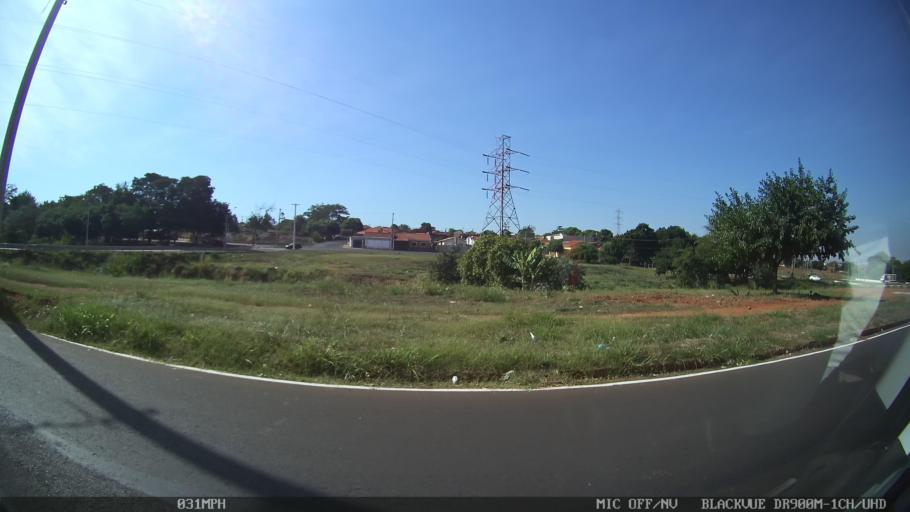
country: BR
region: Sao Paulo
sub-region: Sao Jose Do Rio Preto
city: Sao Jose do Rio Preto
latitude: -20.7894
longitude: -49.4132
